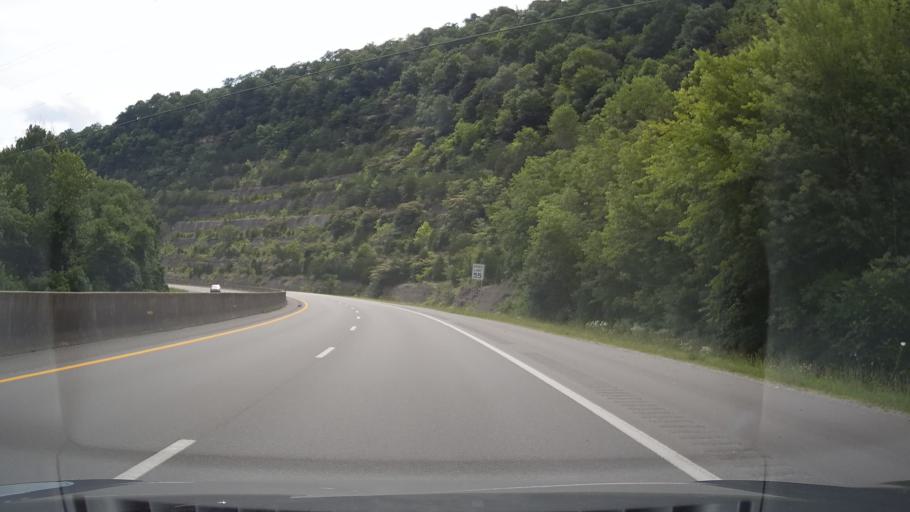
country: US
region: Kentucky
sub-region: Pike County
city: Coal Run Village
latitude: 37.5428
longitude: -82.5864
